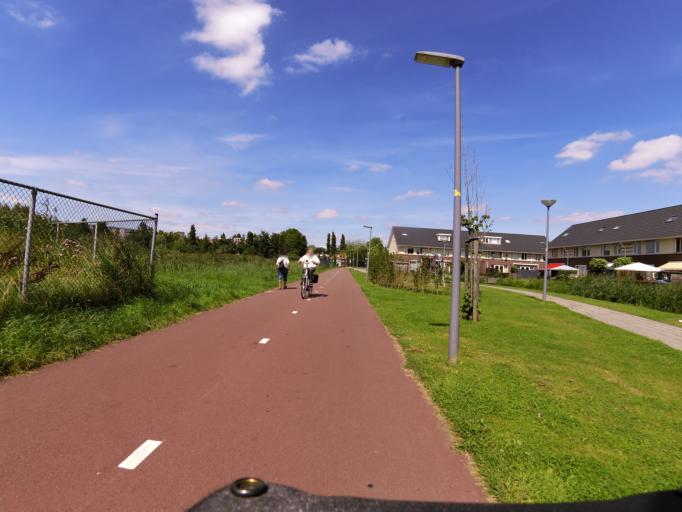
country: NL
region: South Holland
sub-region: Gemeente Barendrecht
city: Barendrecht
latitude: 51.8698
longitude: 4.5292
